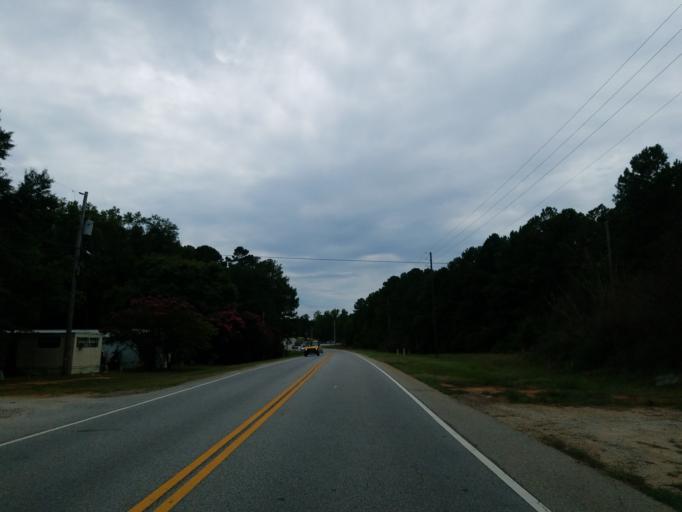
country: US
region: Georgia
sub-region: Clayton County
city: Lovejoy
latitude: 33.4159
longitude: -84.3122
